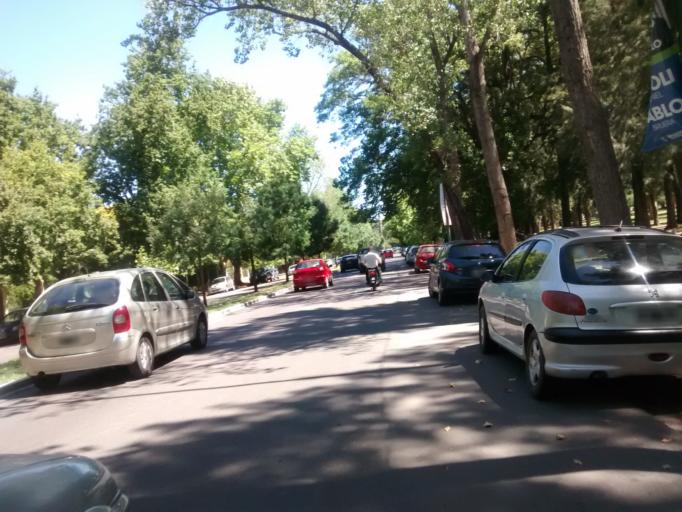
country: AR
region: Buenos Aires
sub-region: Partido de La Plata
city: La Plata
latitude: -34.9076
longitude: -57.9395
